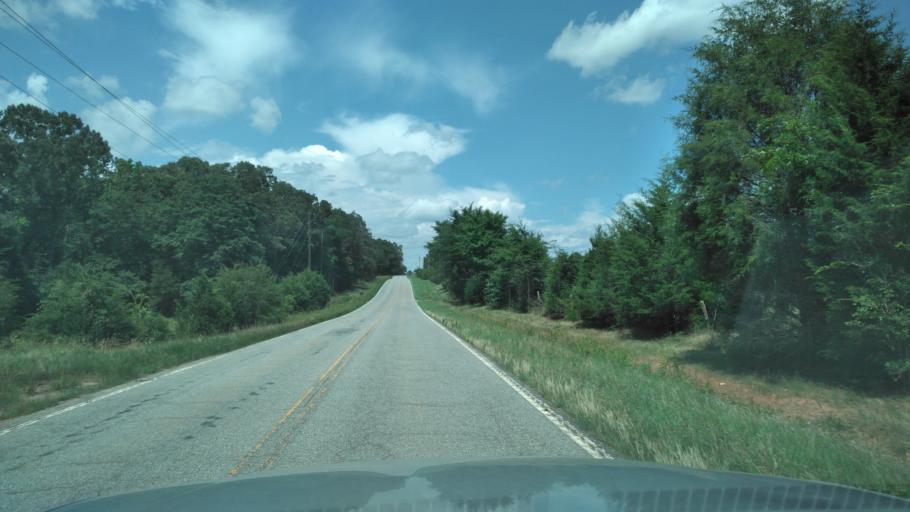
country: US
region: South Carolina
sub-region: Laurens County
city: Laurens
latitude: 34.4816
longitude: -82.1267
